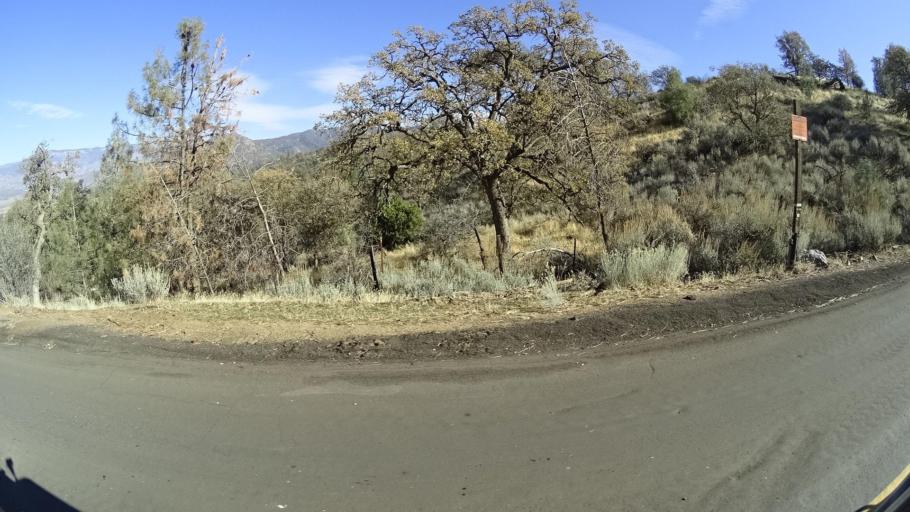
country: US
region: California
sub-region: Kern County
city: Bear Valley Springs
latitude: 35.3670
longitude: -118.5575
